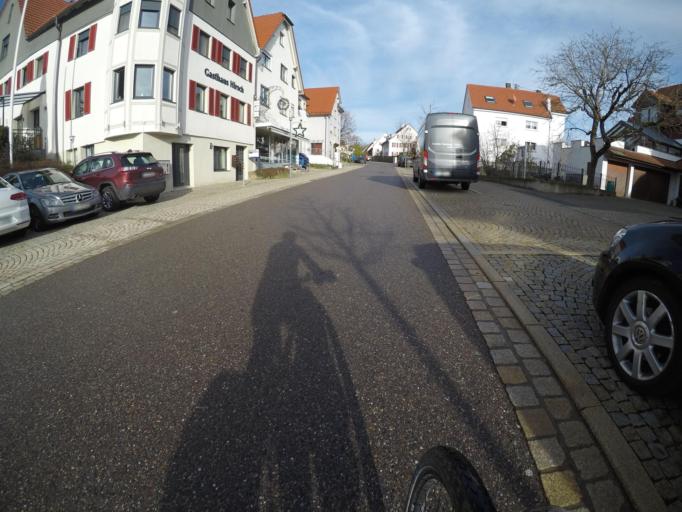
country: DE
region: Baden-Wuerttemberg
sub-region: Regierungsbezirk Stuttgart
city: Baltmannsweiler
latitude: 48.7596
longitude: 9.4529
